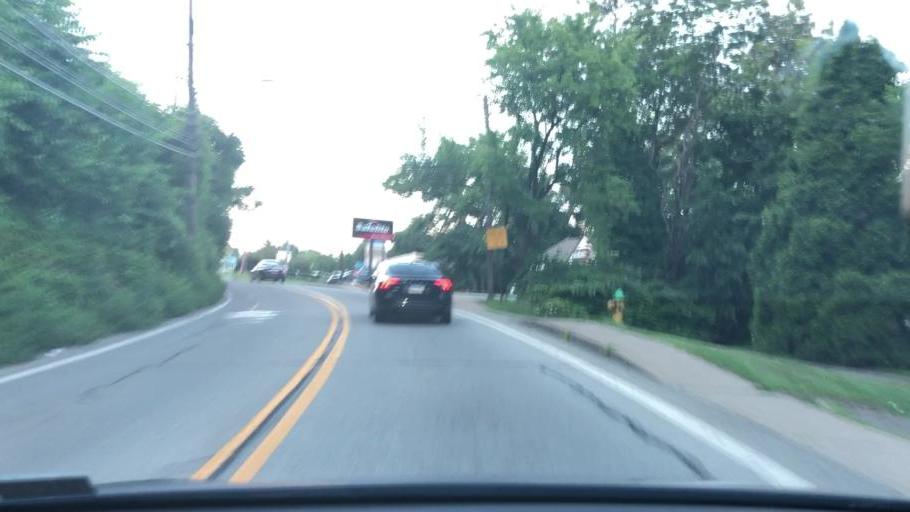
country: US
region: Pennsylvania
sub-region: Allegheny County
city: Churchill
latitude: 40.4634
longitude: -79.8400
